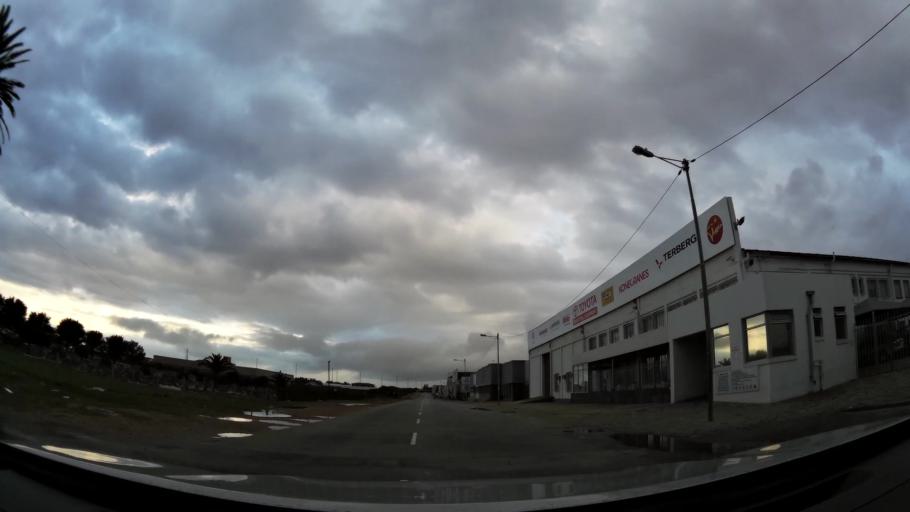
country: ZA
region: Eastern Cape
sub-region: Nelson Mandela Bay Metropolitan Municipality
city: Port Elizabeth
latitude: -33.9249
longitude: 25.6065
